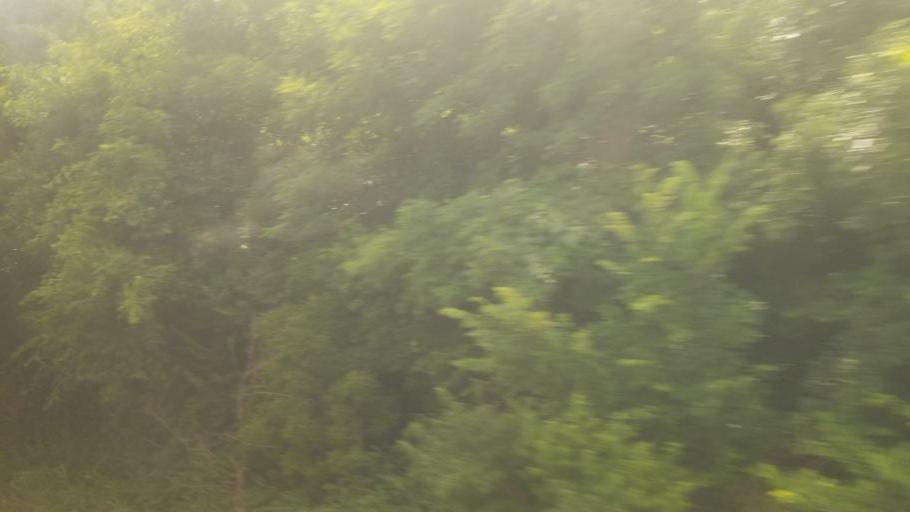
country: US
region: Missouri
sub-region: Jackson County
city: Sugar Creek
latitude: 39.1297
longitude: -94.4343
